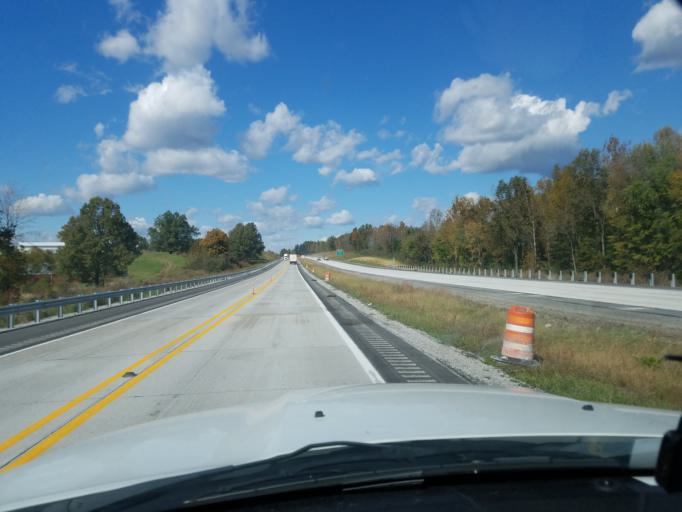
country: US
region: Kentucky
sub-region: Ohio County
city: Beaver Dam
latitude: 37.4390
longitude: -86.8562
